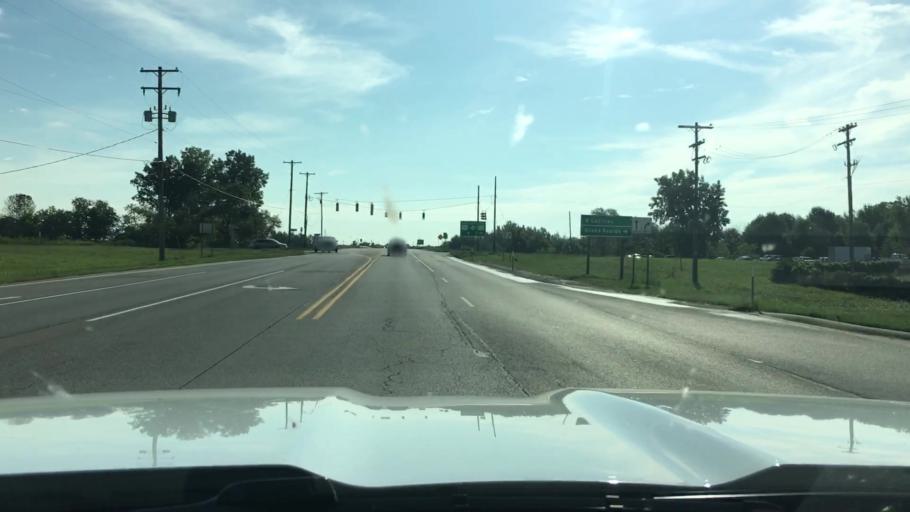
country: US
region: Michigan
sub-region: Kent County
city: Cedar Springs
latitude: 43.2198
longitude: -85.5795
